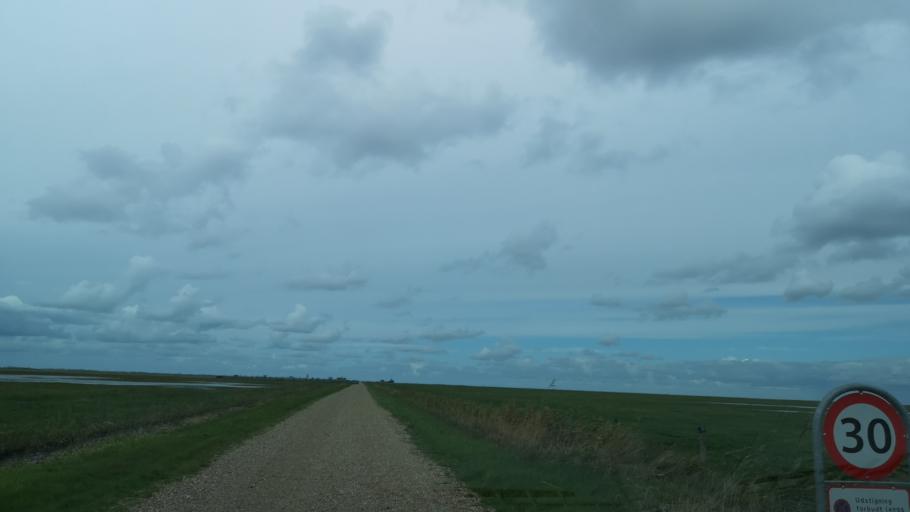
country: DK
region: Central Jutland
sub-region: Ringkobing-Skjern Kommune
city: Hvide Sande
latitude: 55.8741
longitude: 8.2272
